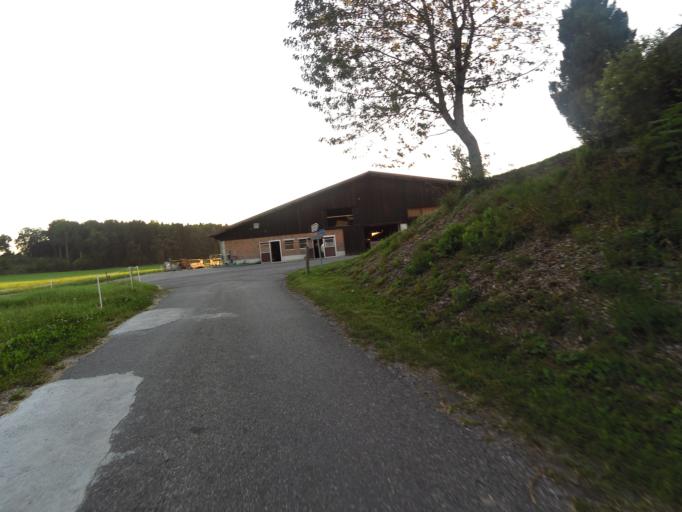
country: CH
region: Thurgau
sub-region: Weinfelden District
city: Wigoltingen
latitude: 47.5713
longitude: 9.0336
